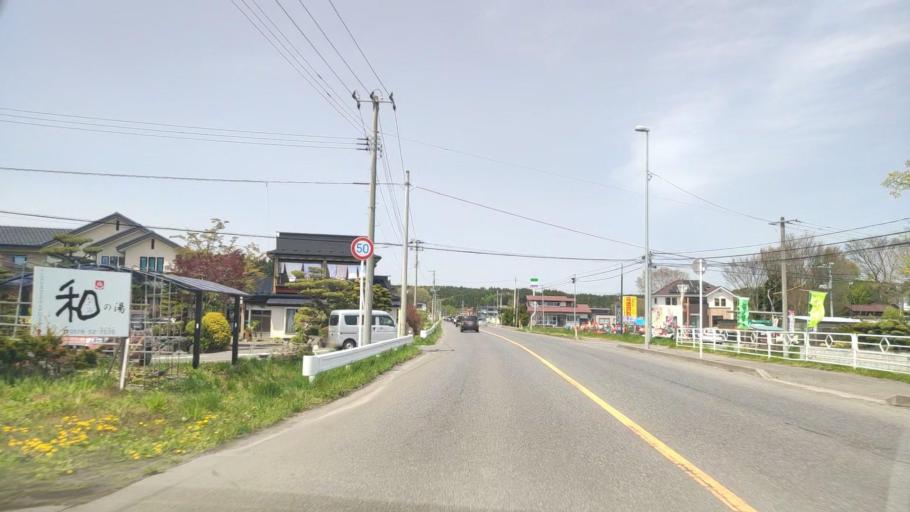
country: JP
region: Aomori
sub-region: Misawa Shi
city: Inuotose
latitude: 40.5580
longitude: 141.3873
